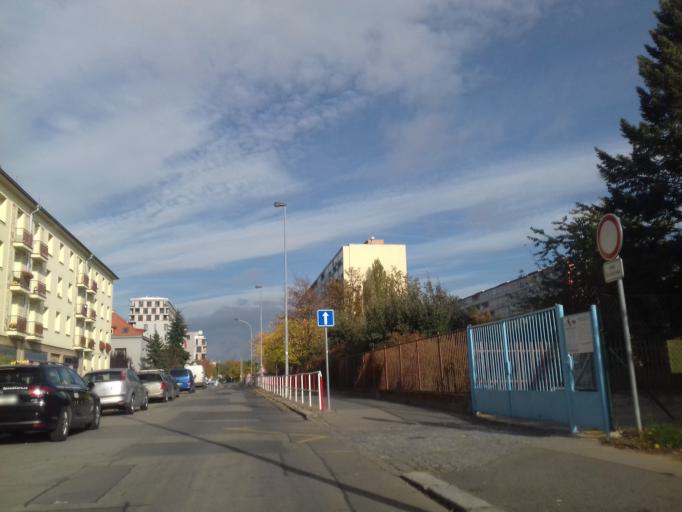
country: CZ
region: Praha
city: Branik
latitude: 50.0457
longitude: 14.4303
